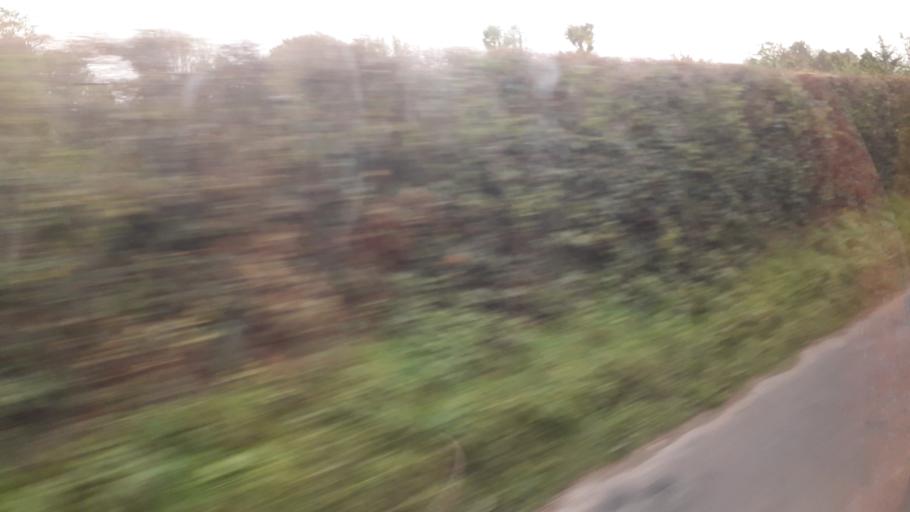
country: IE
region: Munster
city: Ballina
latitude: 52.7982
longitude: -8.4344
